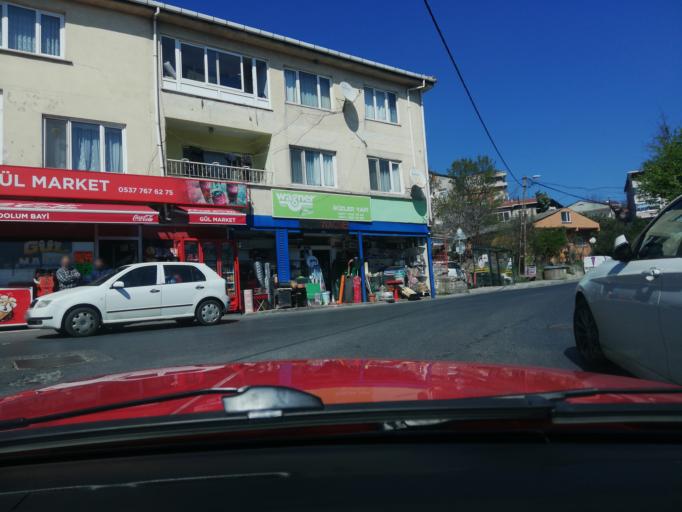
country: TR
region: Istanbul
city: Mahmut Sevket Pasa
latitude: 41.1165
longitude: 29.1149
